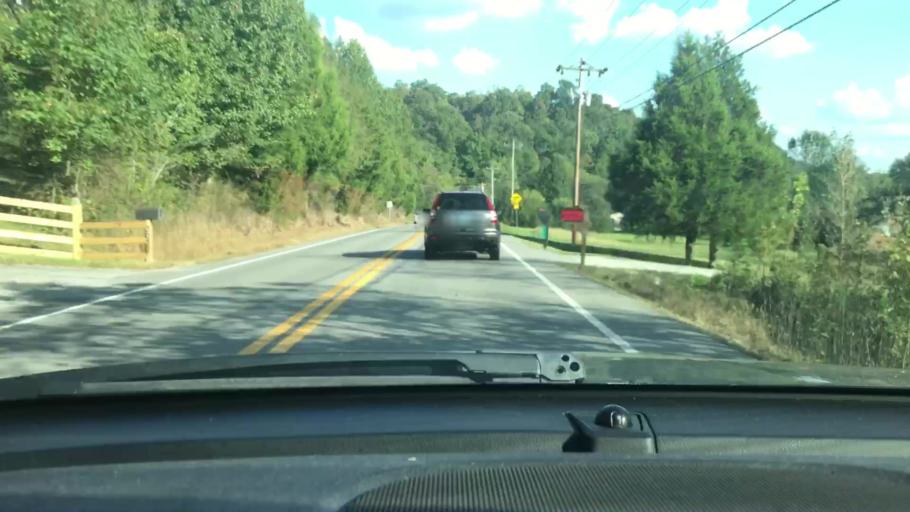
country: US
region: Tennessee
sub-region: Sumner County
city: Shackle Island
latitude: 36.4104
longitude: -86.6376
